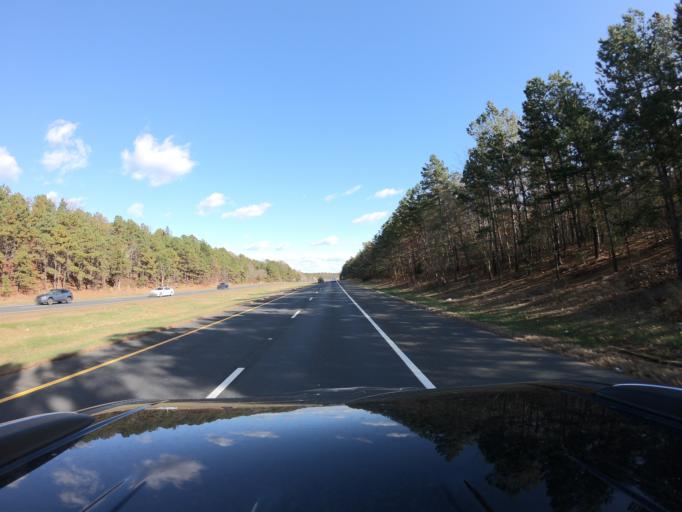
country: US
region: New Jersey
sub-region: Monmouth County
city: Farmingdale
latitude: 40.1669
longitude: -74.1962
